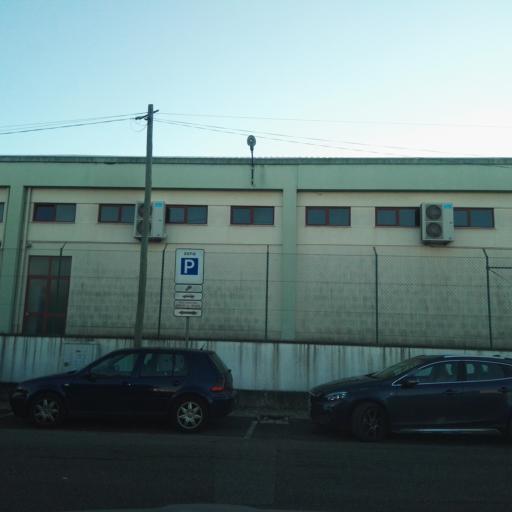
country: PT
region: Lisbon
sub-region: Loures
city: Camarate
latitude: 38.7864
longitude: -9.1258
